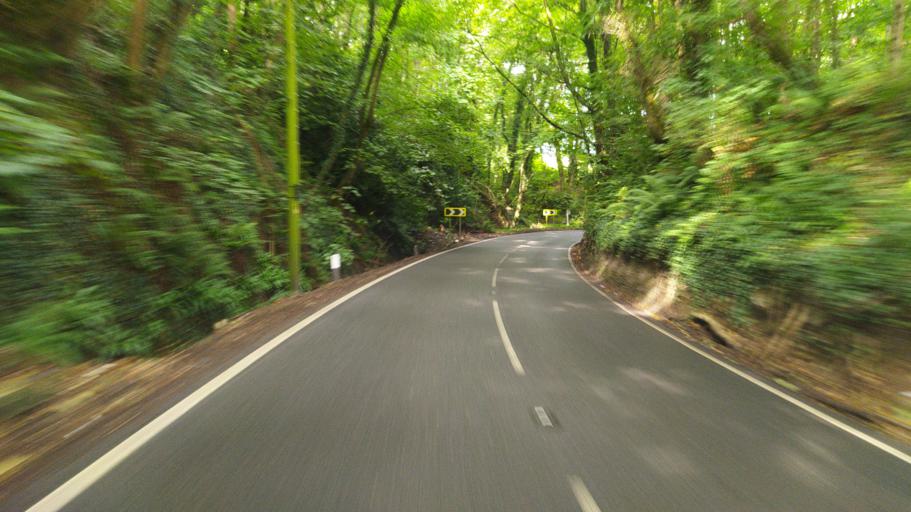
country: GB
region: England
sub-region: Hampshire
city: Petersfield
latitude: 50.9857
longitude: -0.9219
